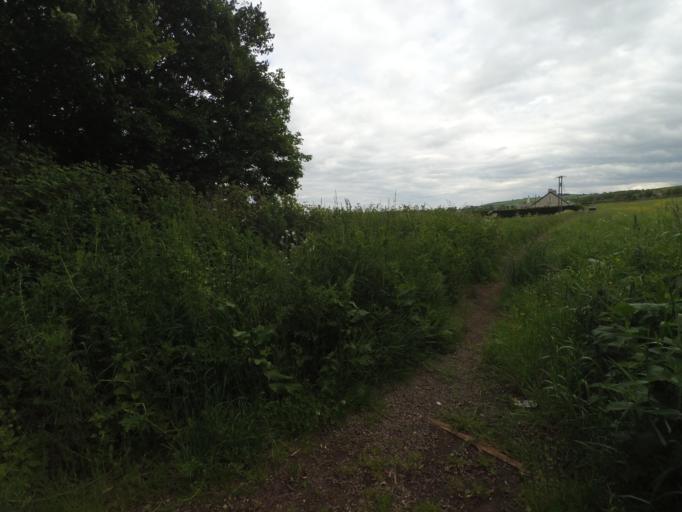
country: GB
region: Scotland
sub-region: East Lothian
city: Musselburgh
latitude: 55.9187
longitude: -3.0323
